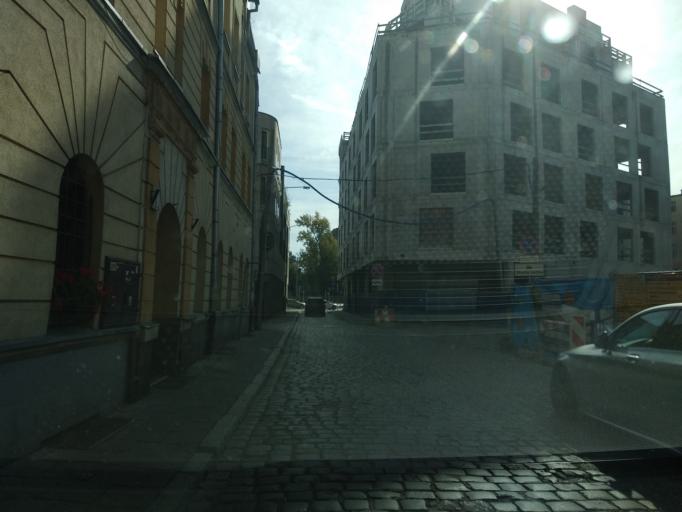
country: PL
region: Lower Silesian Voivodeship
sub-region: Powiat wroclawski
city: Wroclaw
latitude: 51.1181
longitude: 17.0337
